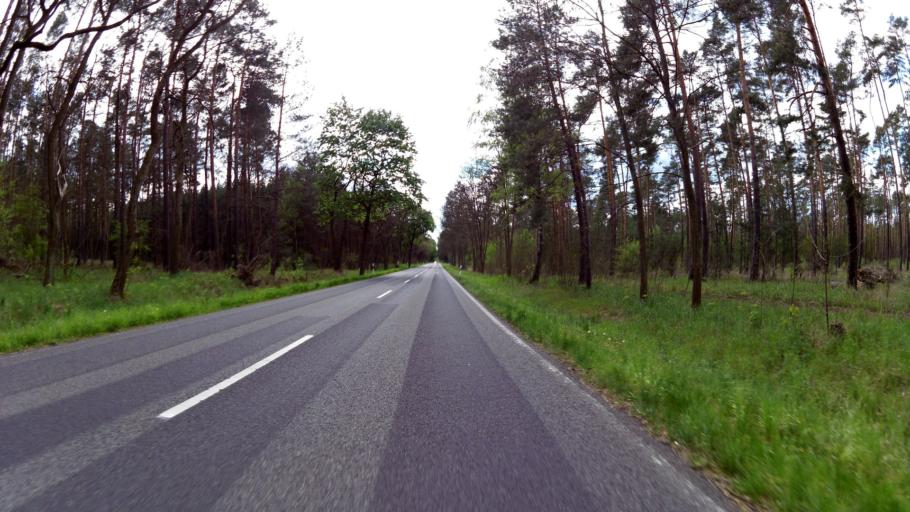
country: DE
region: Brandenburg
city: Rauen
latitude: 52.3457
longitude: 13.9937
